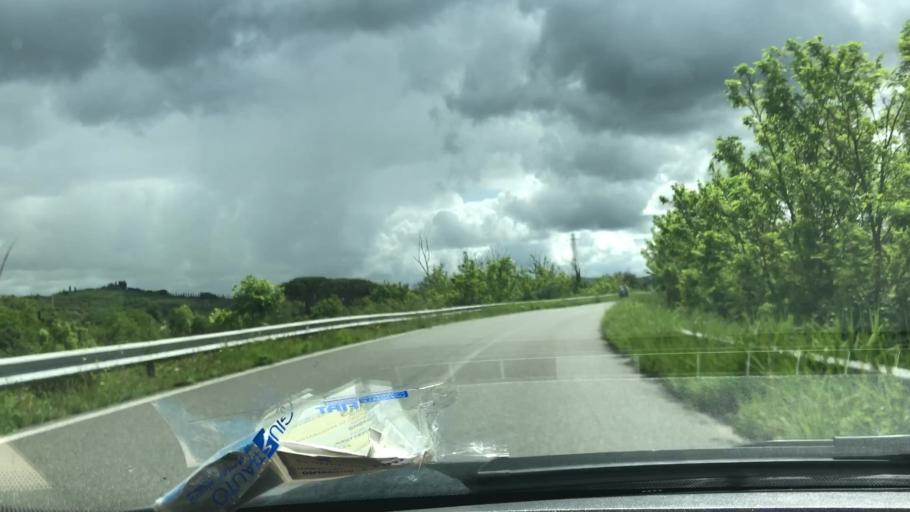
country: IT
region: Tuscany
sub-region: Province of Pisa
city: Saline
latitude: 43.3559
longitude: 10.7827
